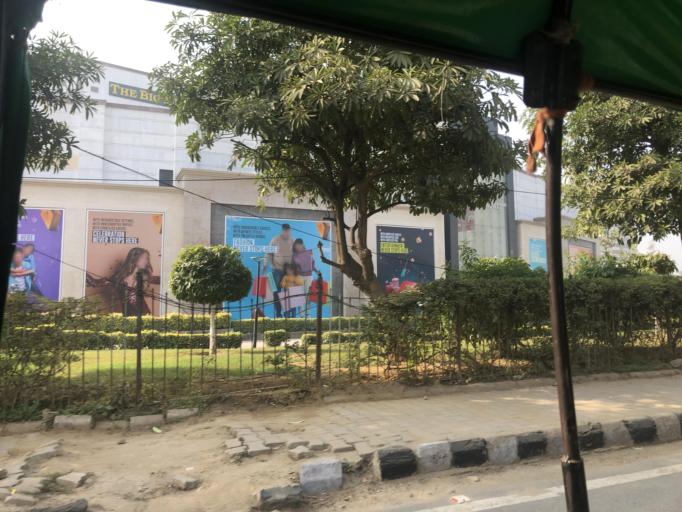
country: IN
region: Haryana
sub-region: Gurgaon
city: Gurgaon
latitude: 28.4453
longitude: 77.0817
